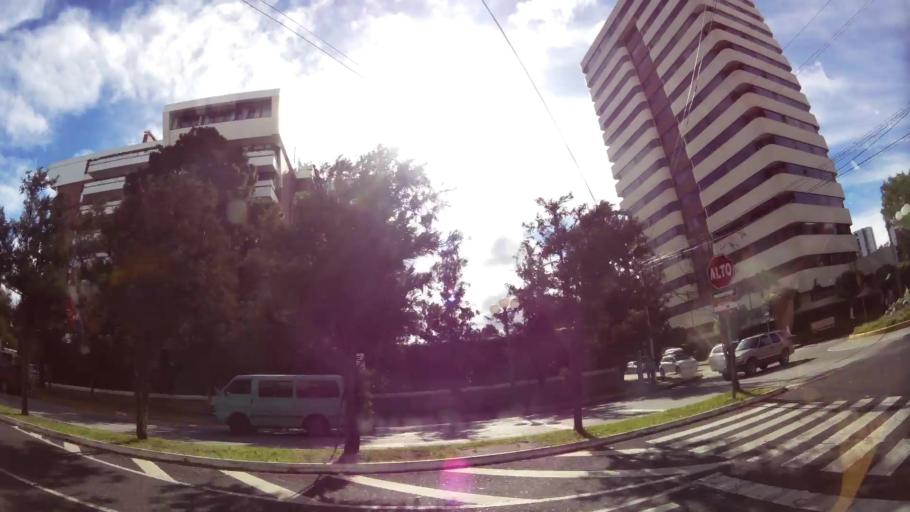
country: GT
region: Guatemala
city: Santa Catarina Pinula
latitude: 14.5845
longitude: -90.5161
